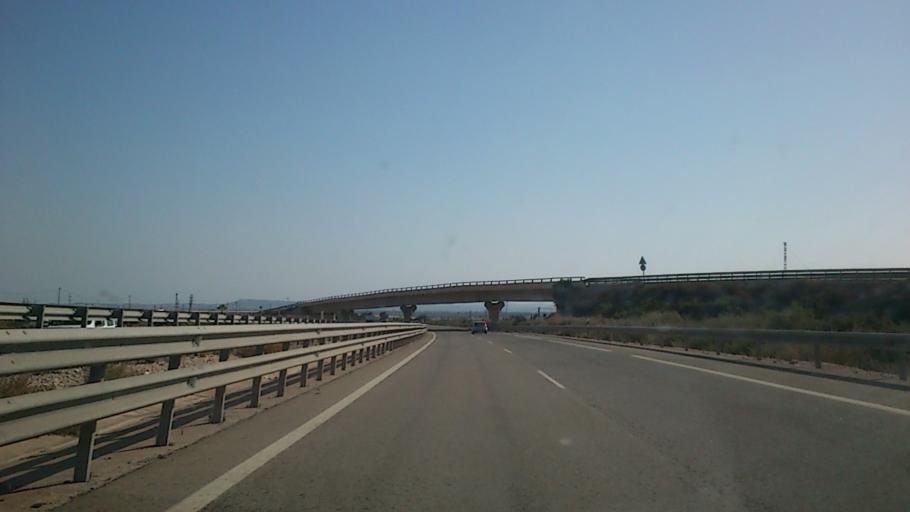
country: ES
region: Valencia
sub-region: Provincia de Alicante
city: Crevillente
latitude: 38.2139
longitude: -0.8168
